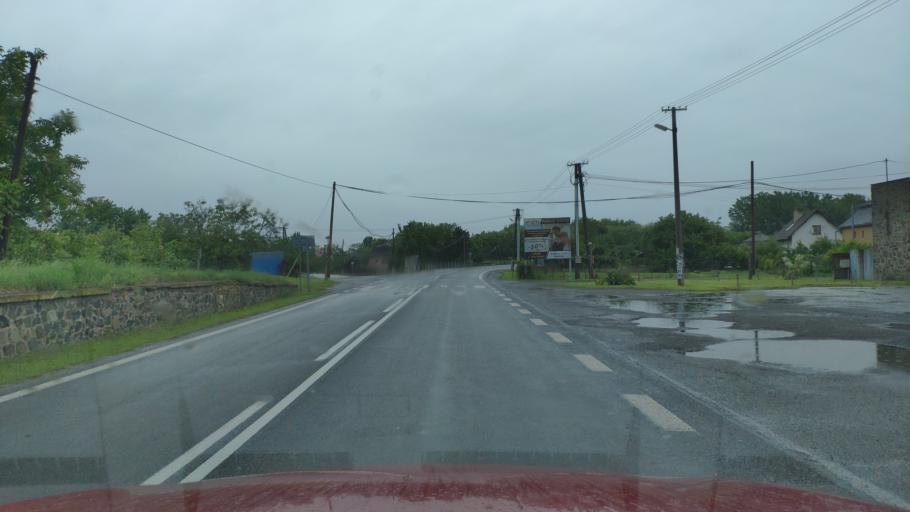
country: HU
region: Borsod-Abauj-Zemplen
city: Karcsa
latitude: 48.4343
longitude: 21.8587
